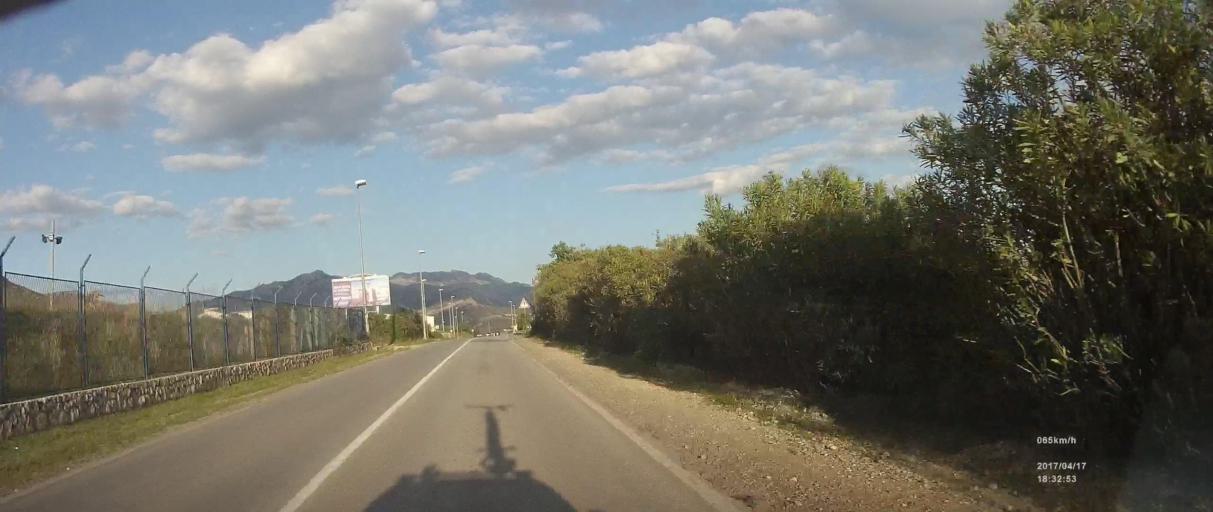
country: HR
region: Splitsko-Dalmatinska
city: Vranjic
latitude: 43.5413
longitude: 16.4518
